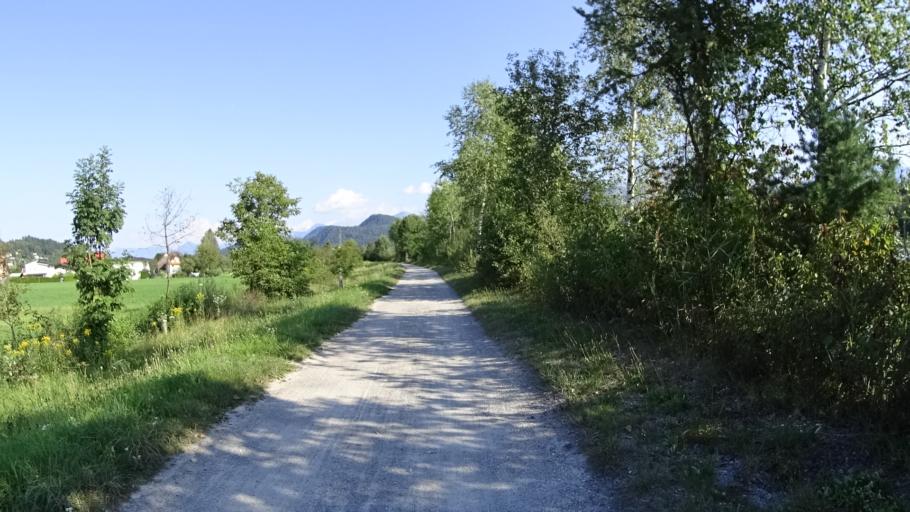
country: AT
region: Carinthia
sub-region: Politischer Bezirk Villach Land
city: Wernberg
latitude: 46.6078
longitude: 13.9381
